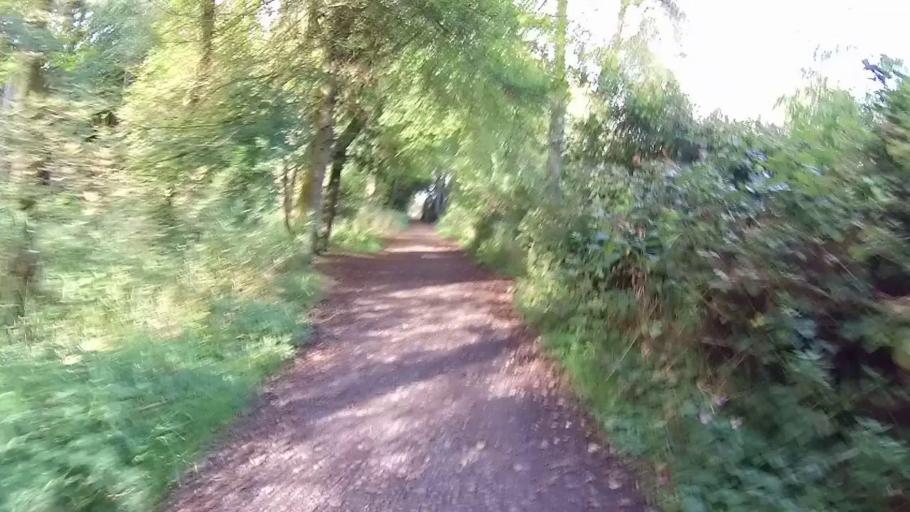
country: GB
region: Scotland
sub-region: Perth and Kinross
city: Kinross
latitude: 56.2111
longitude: -3.4042
